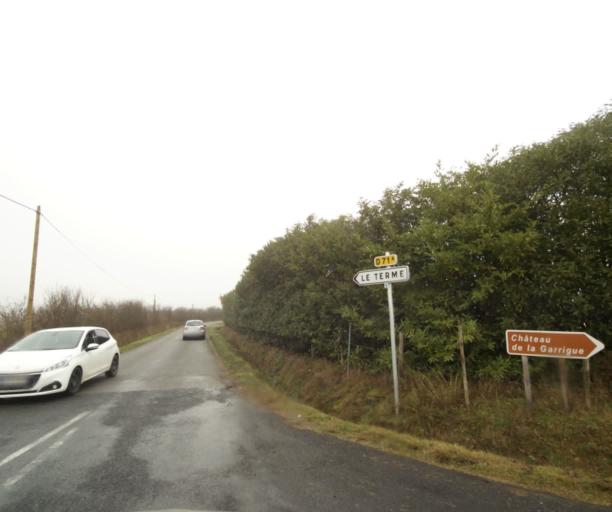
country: FR
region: Midi-Pyrenees
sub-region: Departement du Tarn-et-Garonne
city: Nohic
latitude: 43.8660
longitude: 1.4460
